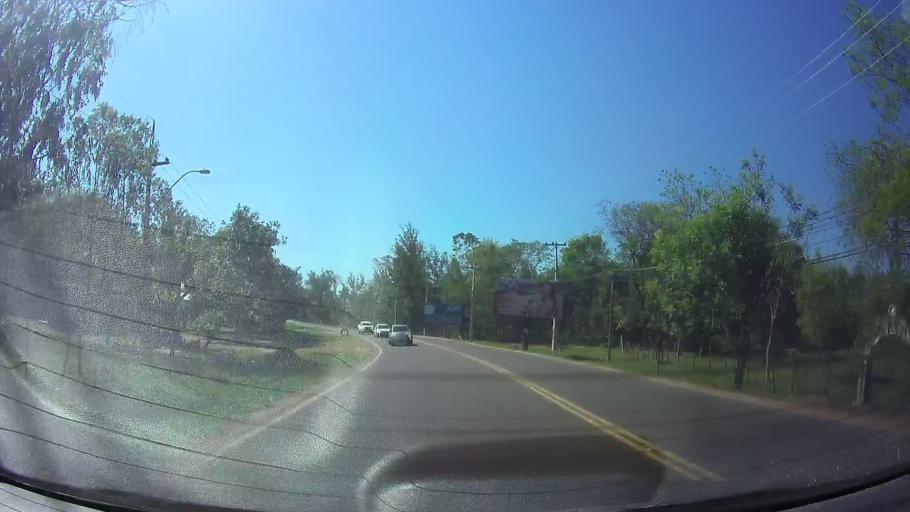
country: PY
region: Cordillera
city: San Bernardino
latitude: -25.3351
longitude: -57.2729
